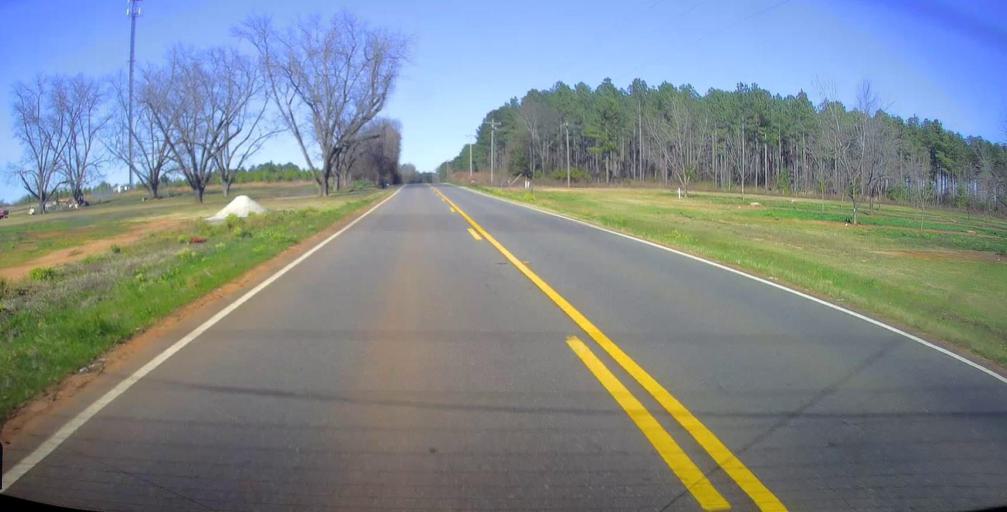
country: US
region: Georgia
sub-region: Macon County
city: Montezuma
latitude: 32.3438
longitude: -84.0196
